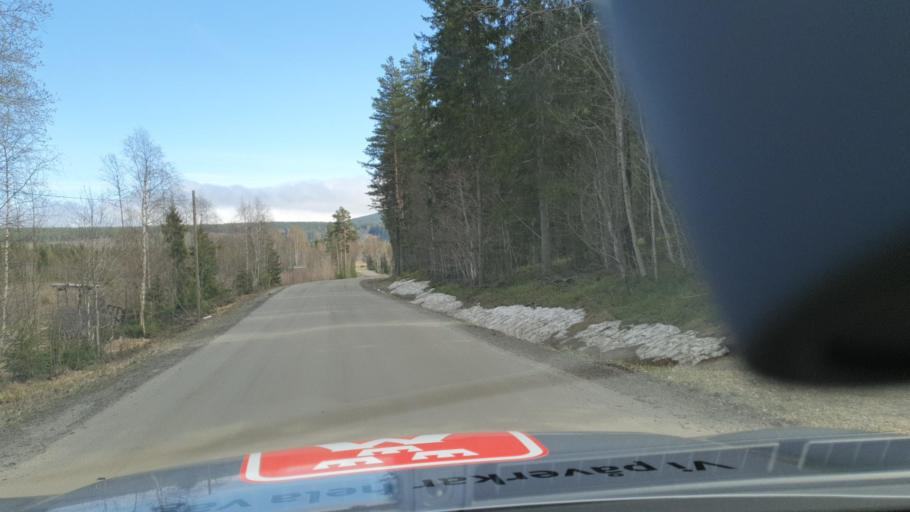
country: SE
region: Vaesterbotten
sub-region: Bjurholms Kommun
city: Bjurholm
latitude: 63.7009
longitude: 18.9284
